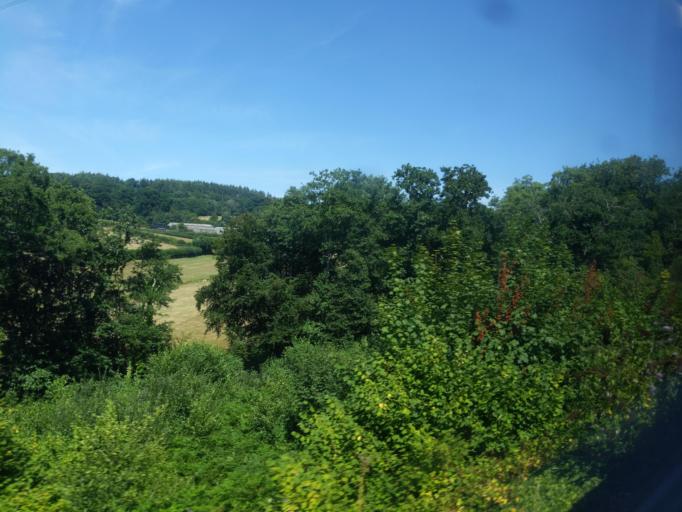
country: GB
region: England
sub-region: Devon
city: Plympton
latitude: 50.3936
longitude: -4.0157
